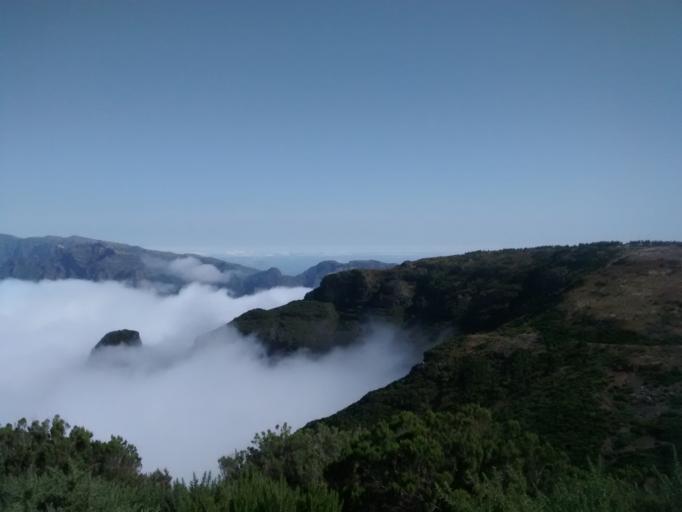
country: PT
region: Madeira
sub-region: Sao Vicente
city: Sao Vicente
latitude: 32.7562
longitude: -17.0549
